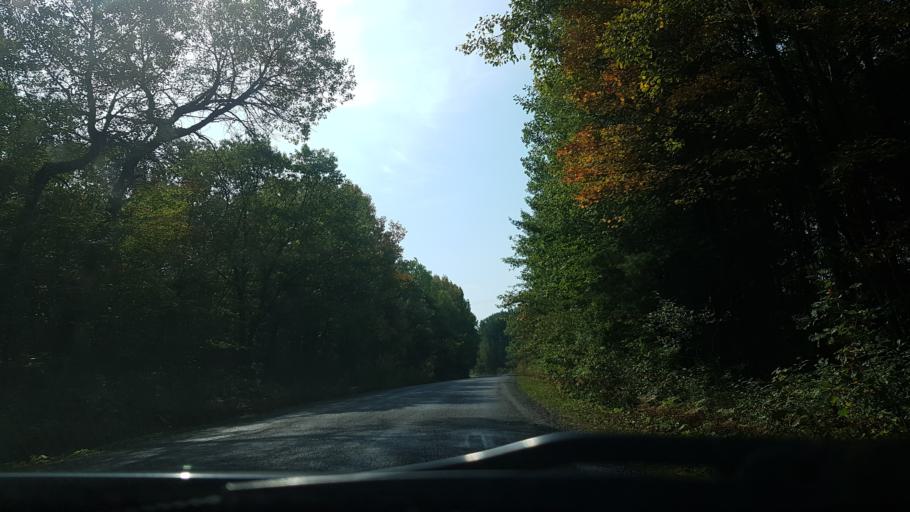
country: CA
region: Ontario
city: Gravenhurst
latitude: 44.8071
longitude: -79.2108
